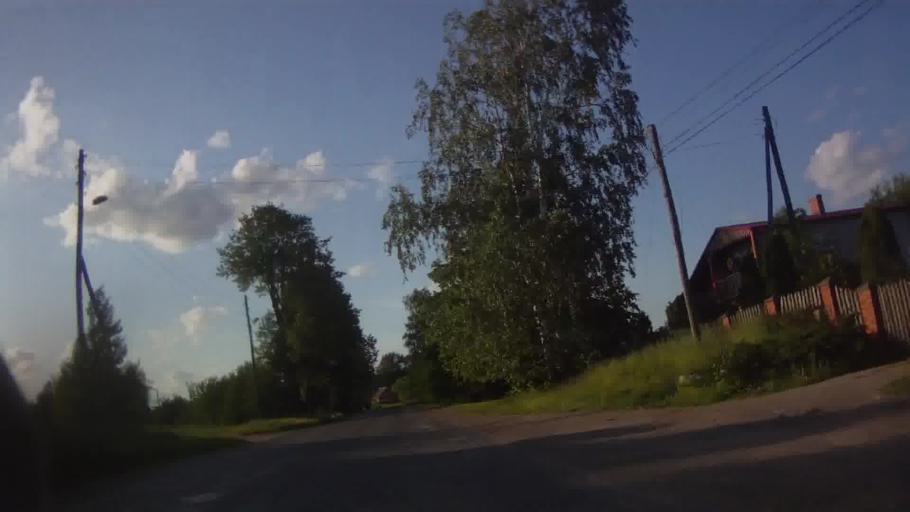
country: LV
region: Rezekne
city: Rezekne
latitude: 56.5257
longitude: 27.3183
